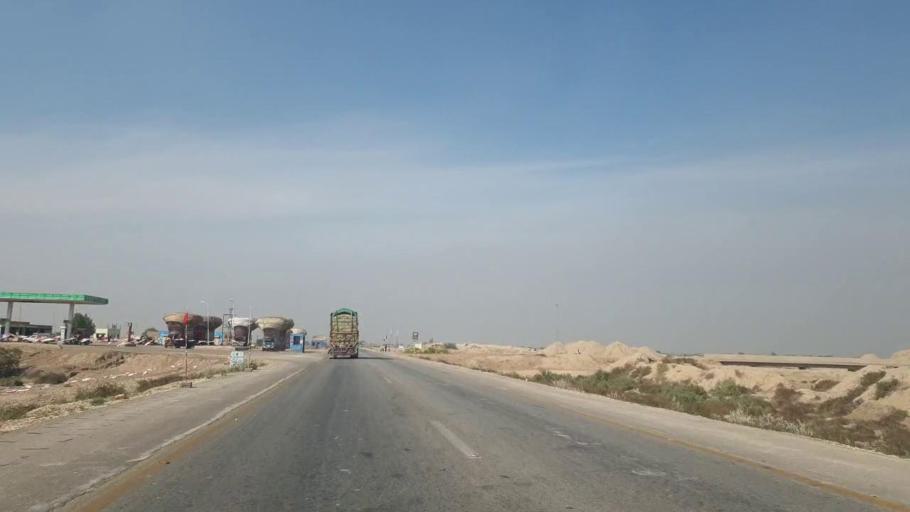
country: PK
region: Sindh
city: Sann
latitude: 25.9513
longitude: 68.1968
